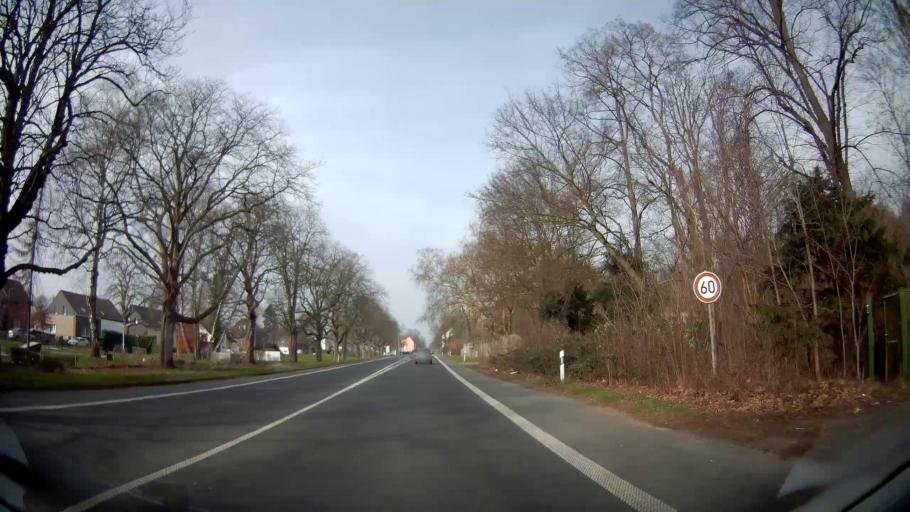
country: DE
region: North Rhine-Westphalia
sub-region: Regierungsbezirk Dusseldorf
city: Moers
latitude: 51.4623
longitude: 6.6982
